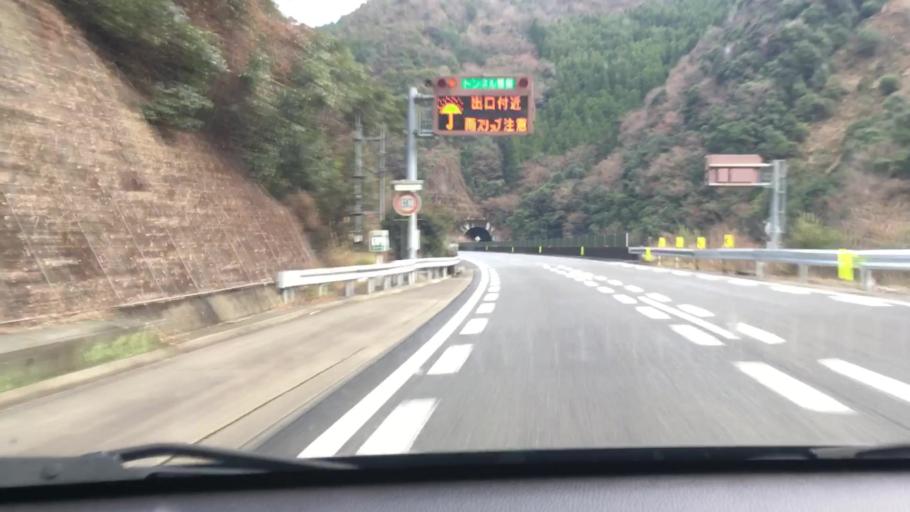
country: JP
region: Kumamoto
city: Hitoyoshi
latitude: 32.3324
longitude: 130.7403
